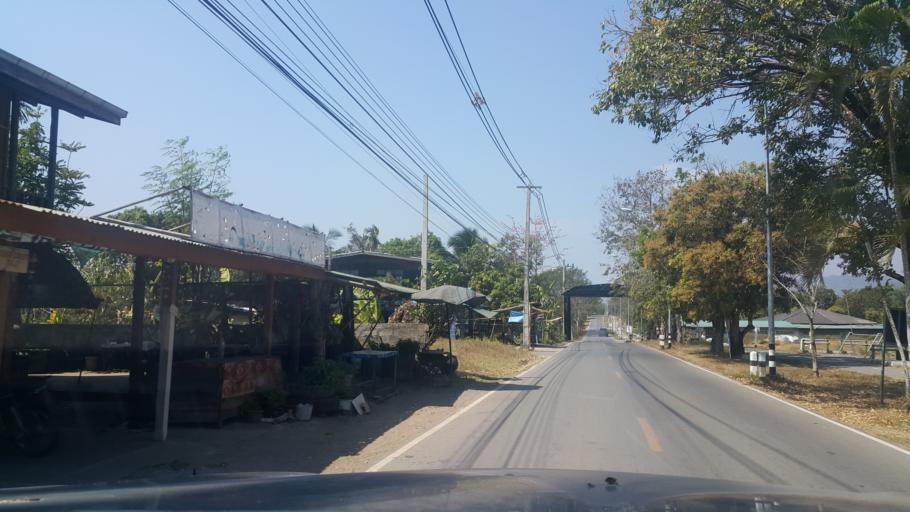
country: TH
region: Nakhon Ratchasima
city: Wang Nam Khiao
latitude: 14.3475
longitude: 101.9404
